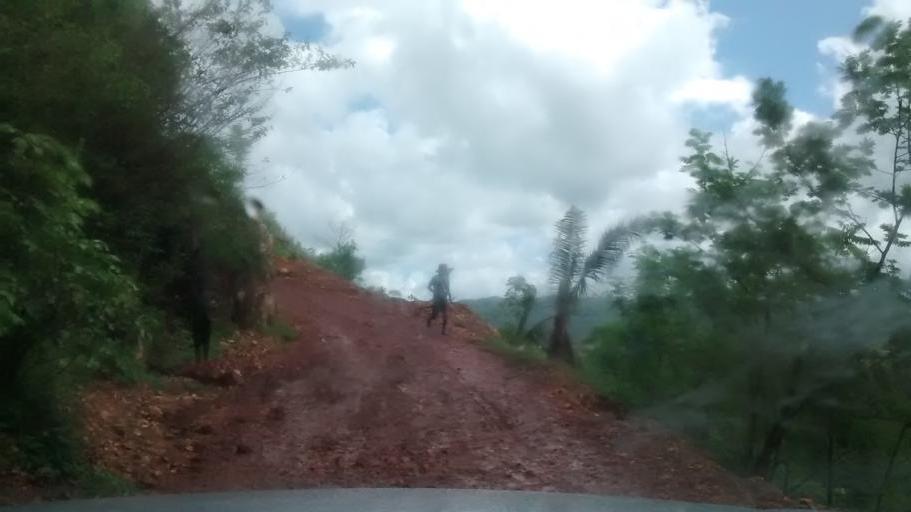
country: HT
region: Grandans
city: Corail
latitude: 18.5374
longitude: -73.9290
